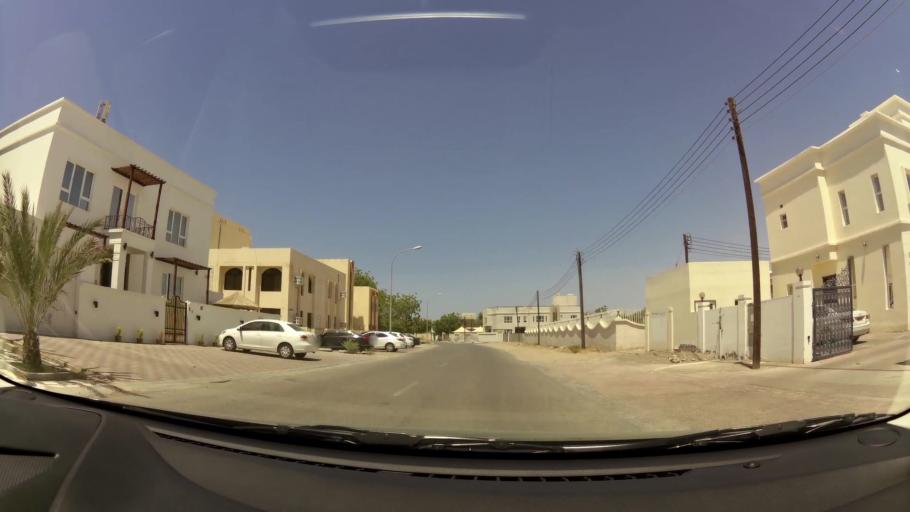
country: OM
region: Muhafazat Masqat
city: As Sib al Jadidah
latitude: 23.6204
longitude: 58.2289
